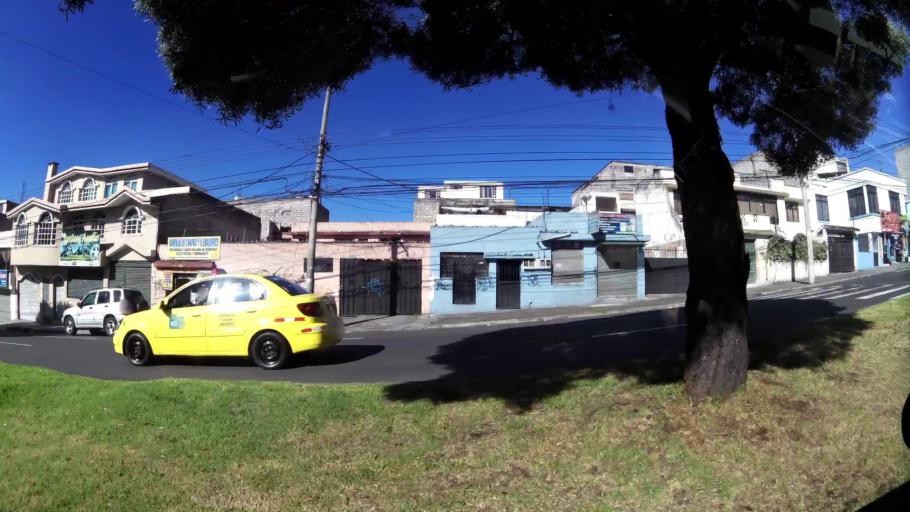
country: EC
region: Pichincha
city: Quito
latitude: -0.2504
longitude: -78.5346
